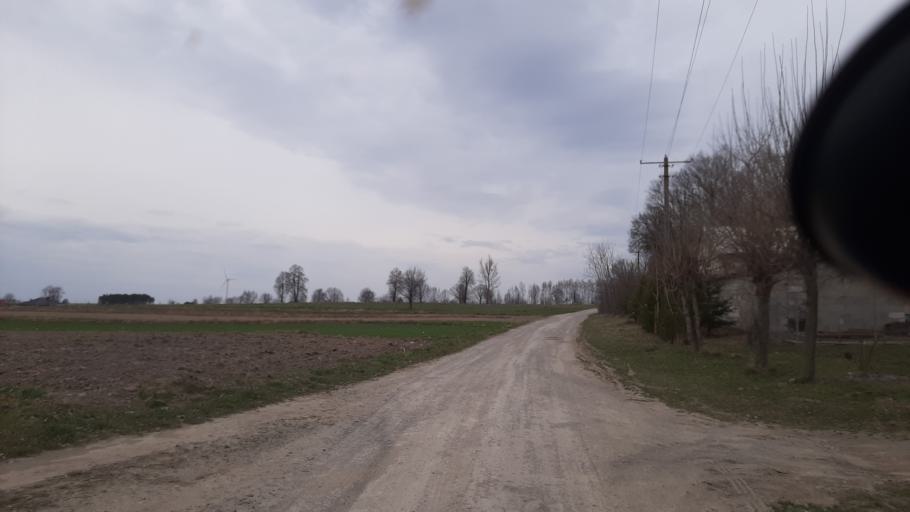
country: PL
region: Lublin Voivodeship
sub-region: Powiat lubartowski
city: Abramow
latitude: 51.4466
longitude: 22.3353
